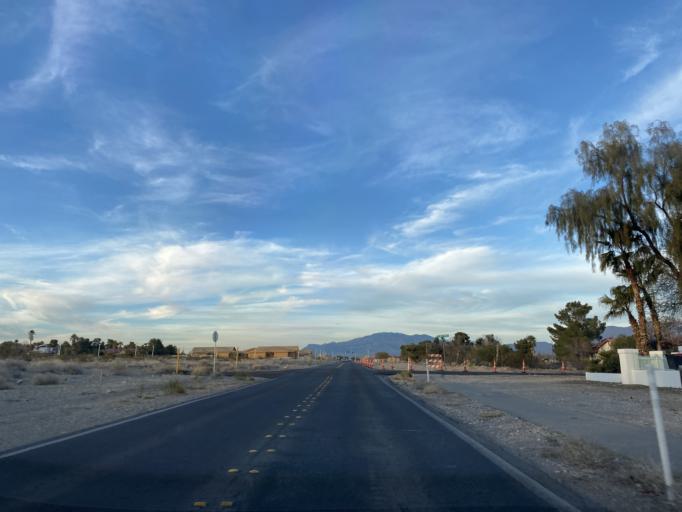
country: US
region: Nevada
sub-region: Clark County
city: Summerlin South
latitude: 36.2660
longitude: -115.2973
